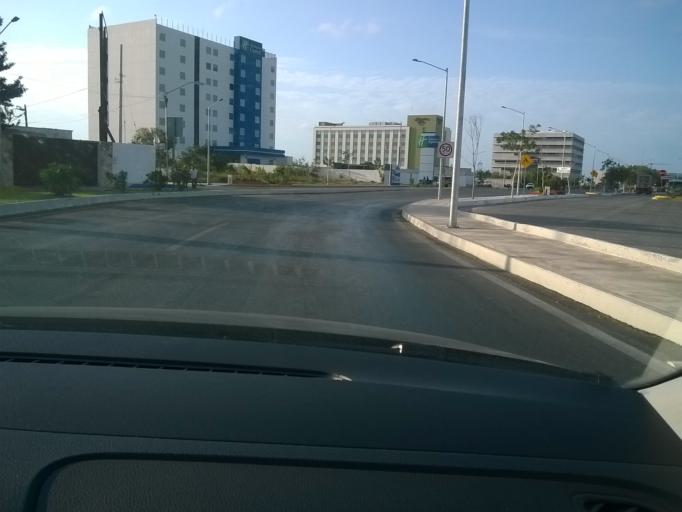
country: MX
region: Yucatan
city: Merida
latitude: 21.0331
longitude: -89.6314
